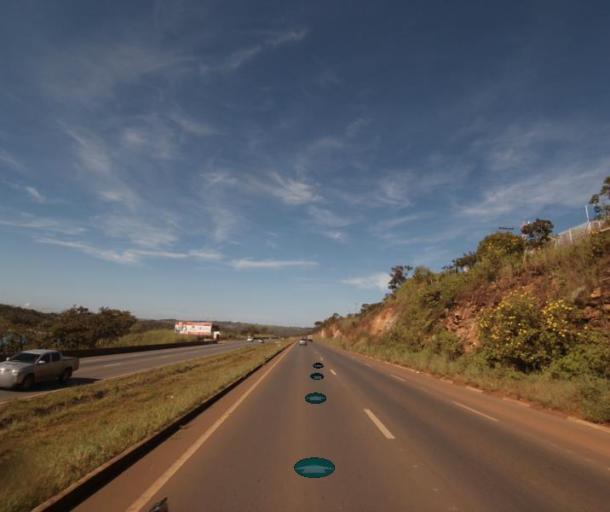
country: BR
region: Federal District
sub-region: Brasilia
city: Brasilia
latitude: -15.7744
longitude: -48.2321
